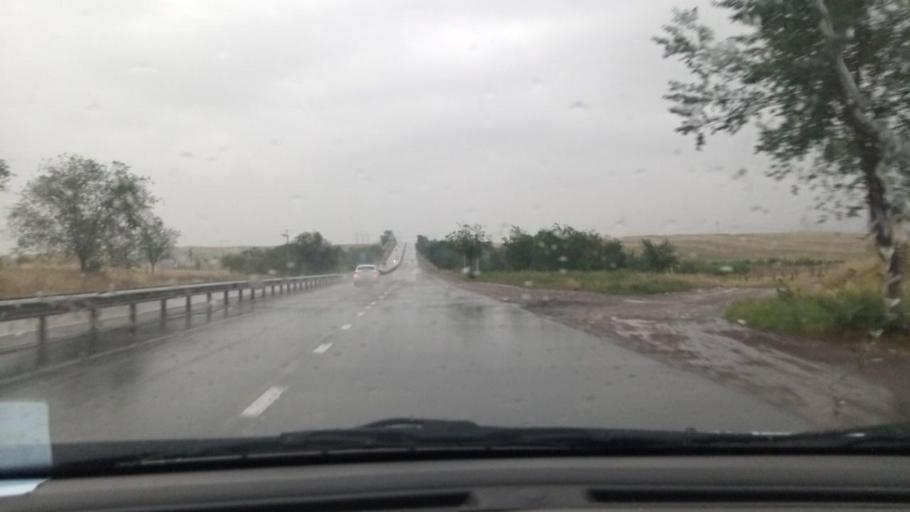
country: UZ
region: Toshkent
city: Ohangaron
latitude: 40.9546
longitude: 69.5655
